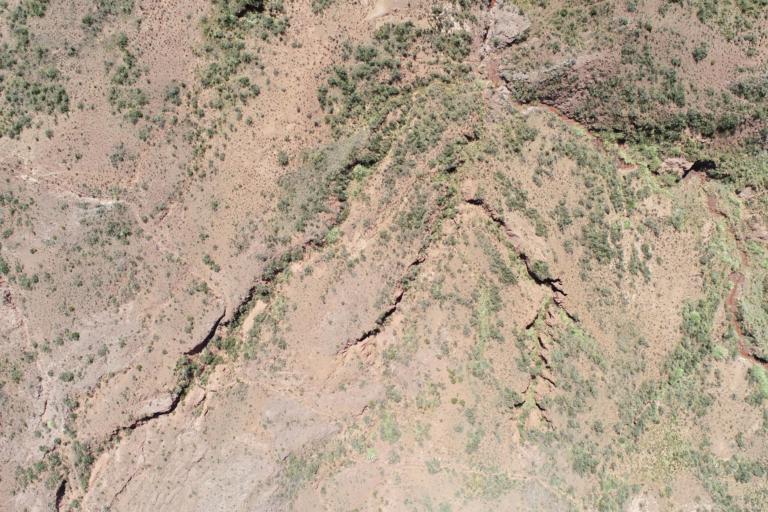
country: BO
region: La Paz
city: Tiahuanaco
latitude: -16.5992
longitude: -68.7553
